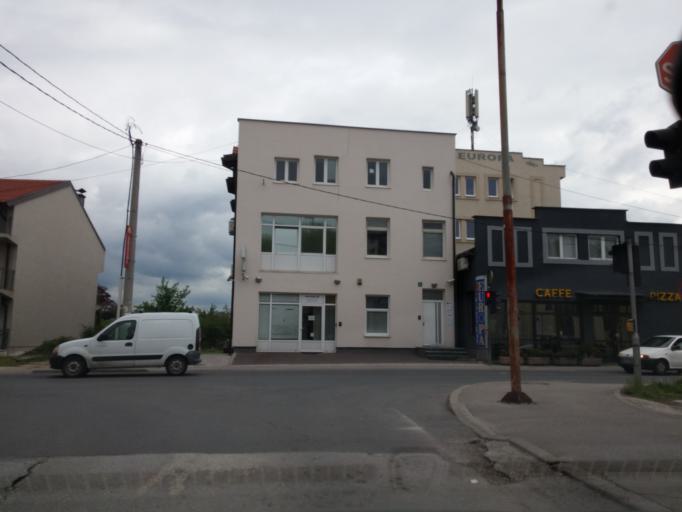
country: BA
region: Federation of Bosnia and Herzegovina
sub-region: Kanton Sarajevo
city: Sarajevo
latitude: 43.8410
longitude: 18.3375
